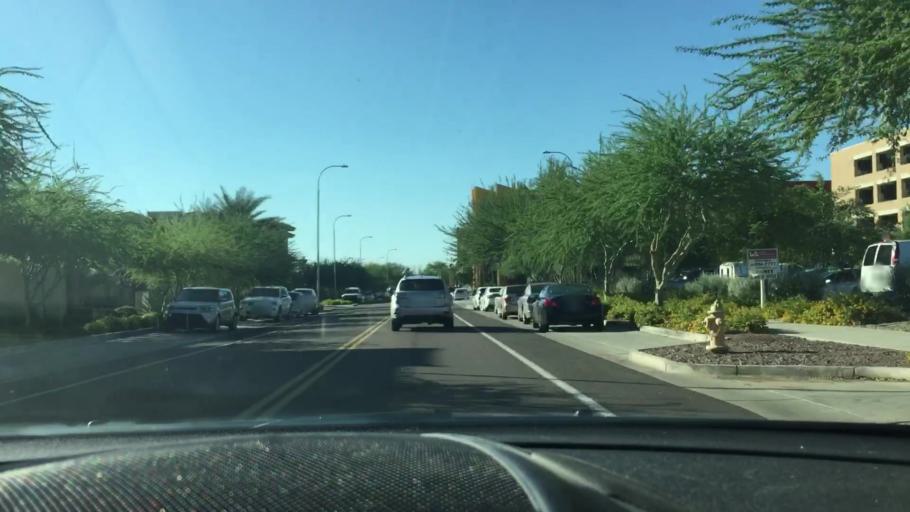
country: US
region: Arizona
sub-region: Maricopa County
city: Scottsdale
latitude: 33.4645
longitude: -111.9219
